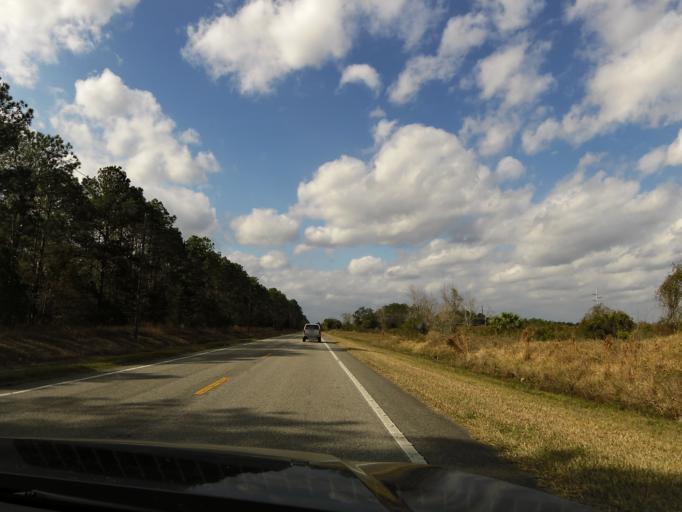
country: US
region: Florida
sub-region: Volusia County
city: De Leon Springs
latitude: 29.1667
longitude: -81.3947
